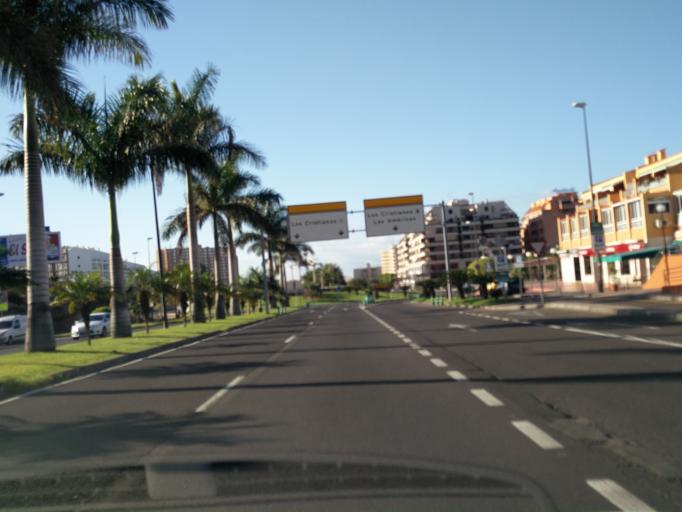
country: ES
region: Canary Islands
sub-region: Provincia de Santa Cruz de Tenerife
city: Playa de las Americas
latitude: 28.0569
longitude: -16.7117
